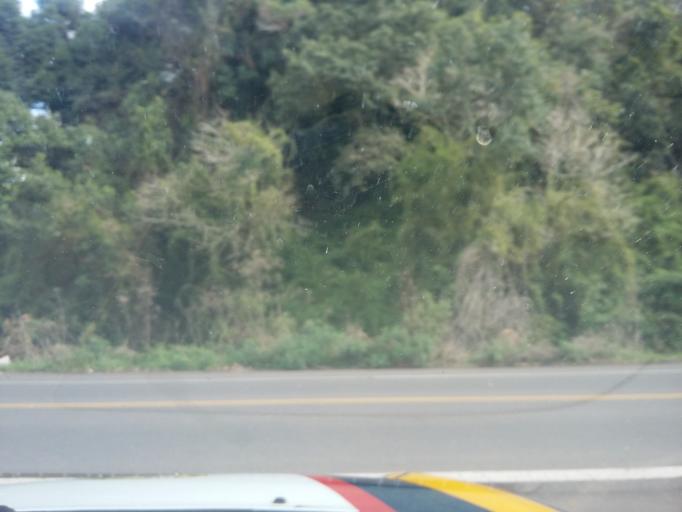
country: BR
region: Rio Grande do Sul
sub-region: Sao Marcos
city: Sao Marcos
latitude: -28.7893
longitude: -51.0950
